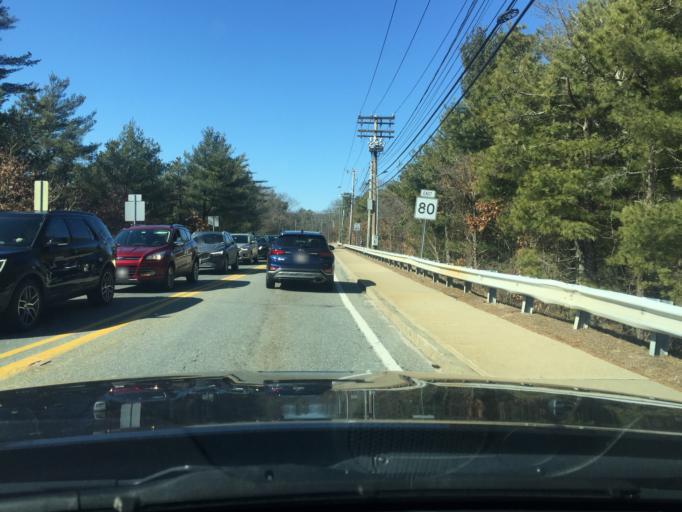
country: US
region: Massachusetts
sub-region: Plymouth County
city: North Plymouth
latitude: 41.9444
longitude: -70.7067
